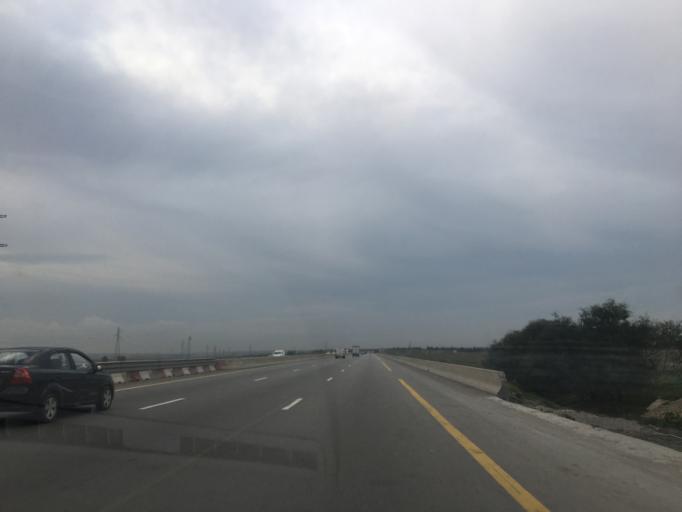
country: DZ
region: Bouira
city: Bouira
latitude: 36.3274
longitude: 3.9824
